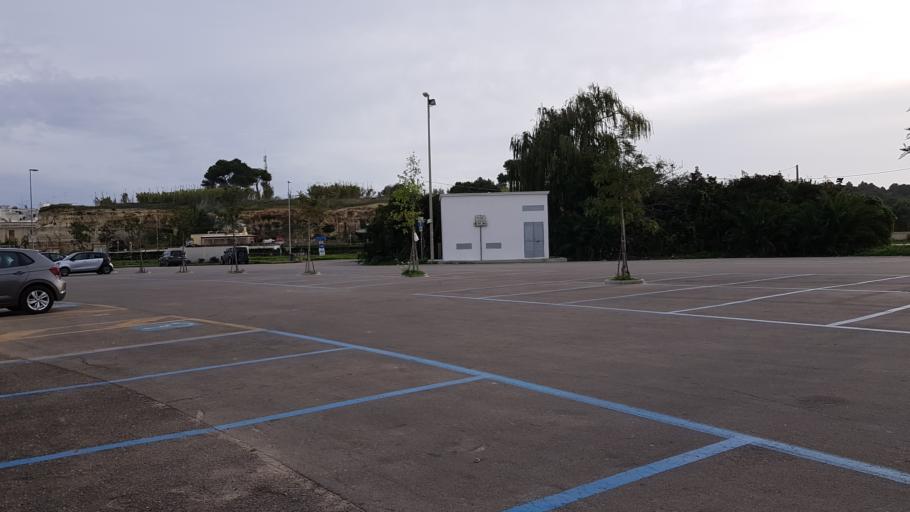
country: IT
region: Apulia
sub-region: Provincia di Lecce
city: Otranto
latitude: 40.1477
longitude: 18.4861
